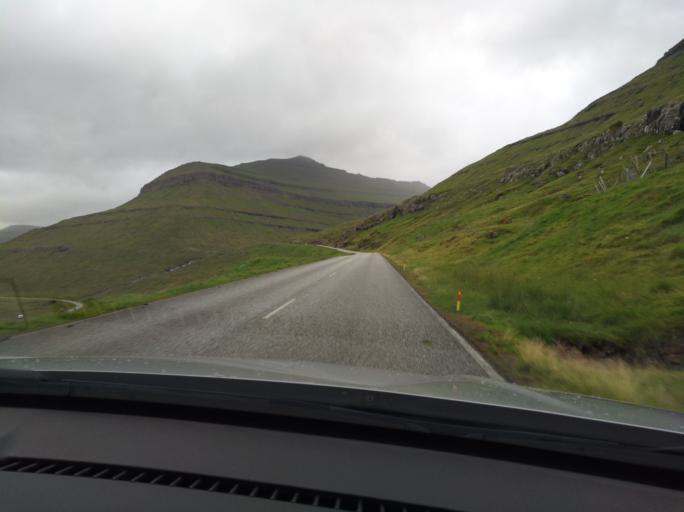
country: FO
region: Eysturoy
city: Fuglafjordur
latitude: 62.2171
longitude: -6.8647
